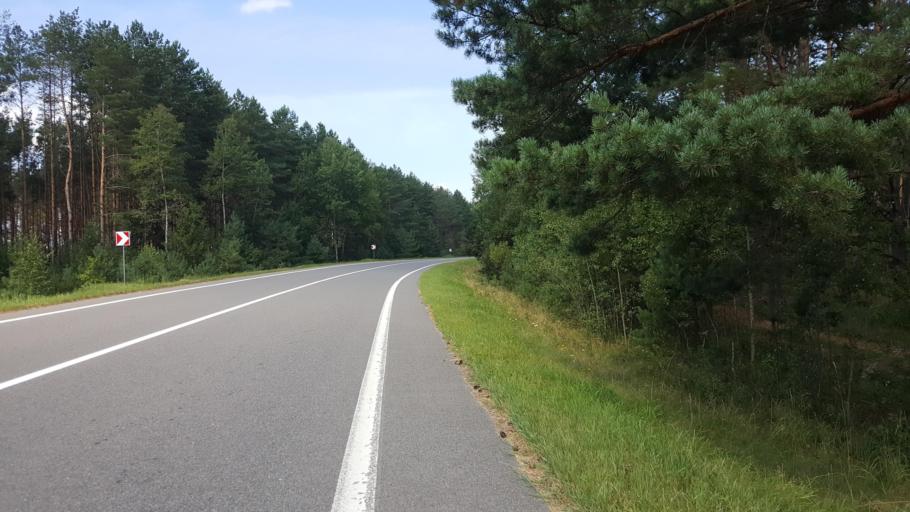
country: BY
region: Brest
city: Kamyanyuki
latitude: 52.5603
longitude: 23.6248
